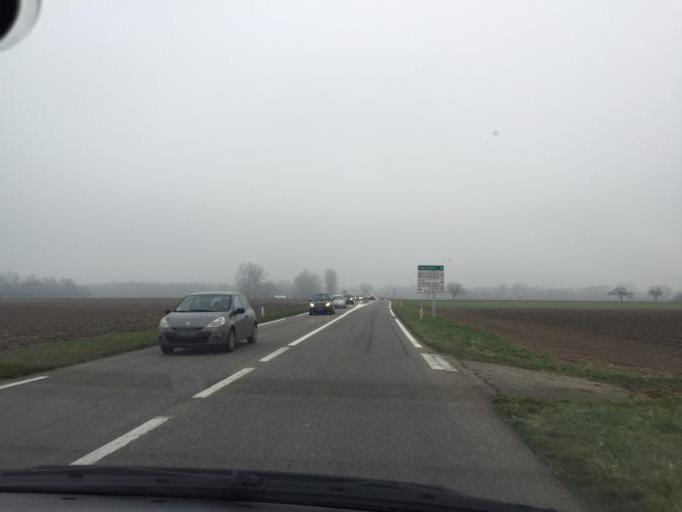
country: FR
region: Alsace
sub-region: Departement du Haut-Rhin
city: Andolsheim
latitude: 48.0580
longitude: 7.4326
